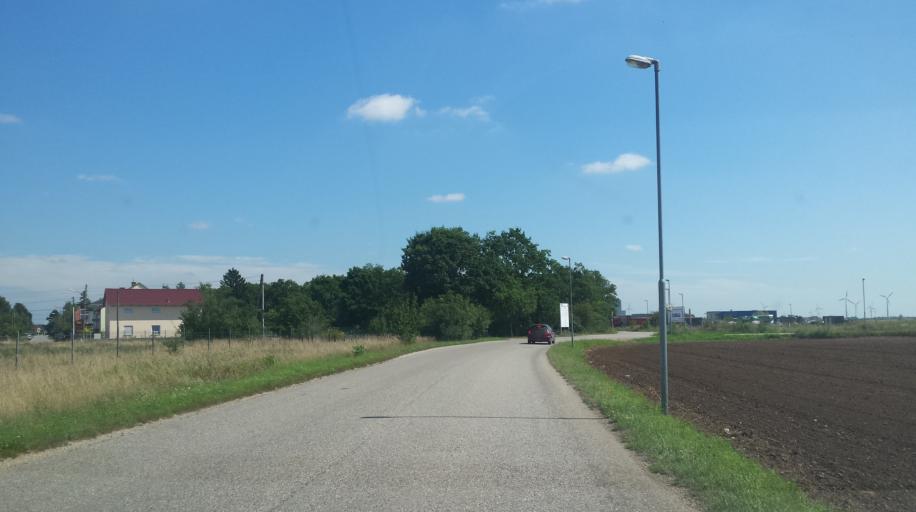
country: AT
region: Lower Austria
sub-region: Politischer Bezirk Ganserndorf
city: Parbasdorf
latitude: 48.3089
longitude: 16.6133
